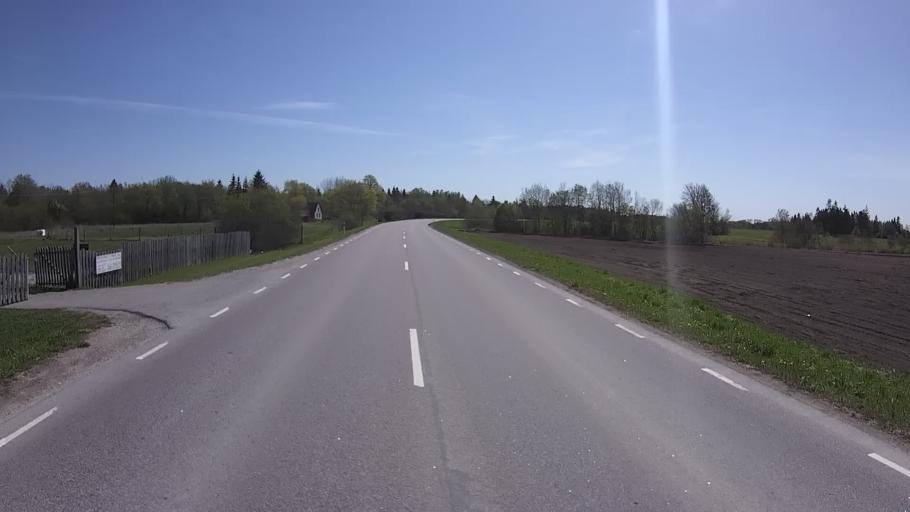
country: EE
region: Harju
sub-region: Keila linn
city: Keila
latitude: 59.3062
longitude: 24.3235
